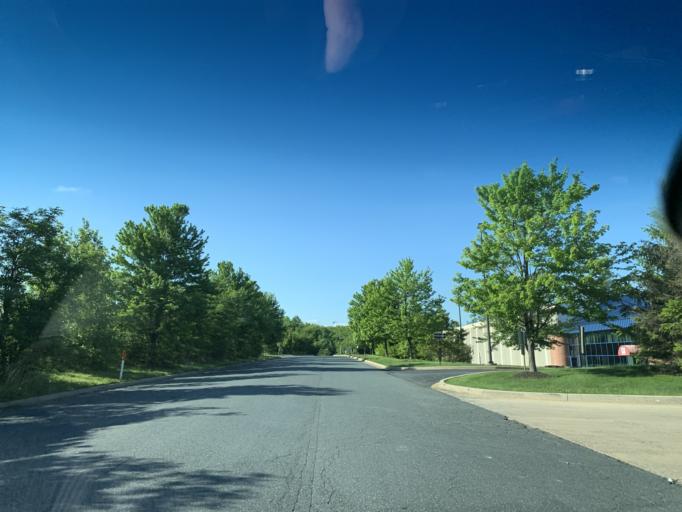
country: US
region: Maryland
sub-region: Harford County
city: Riverside
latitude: 39.4826
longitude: -76.2309
